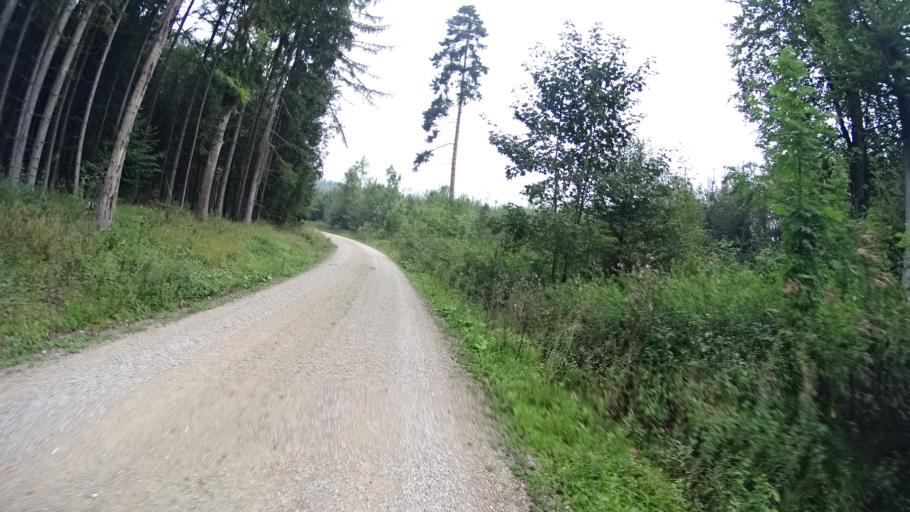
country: DE
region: Bavaria
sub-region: Upper Bavaria
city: Stammham
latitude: 48.8609
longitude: 11.4986
